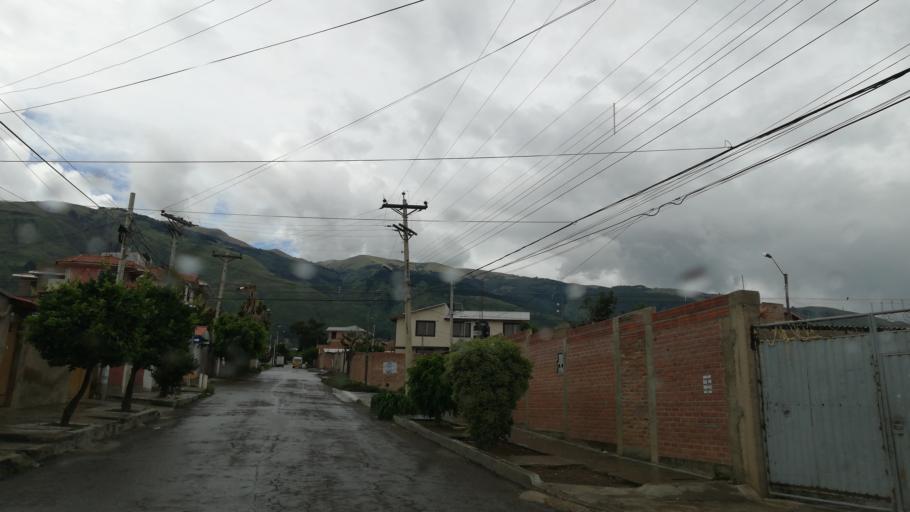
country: BO
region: Cochabamba
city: Cochabamba
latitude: -17.3534
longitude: -66.1769
